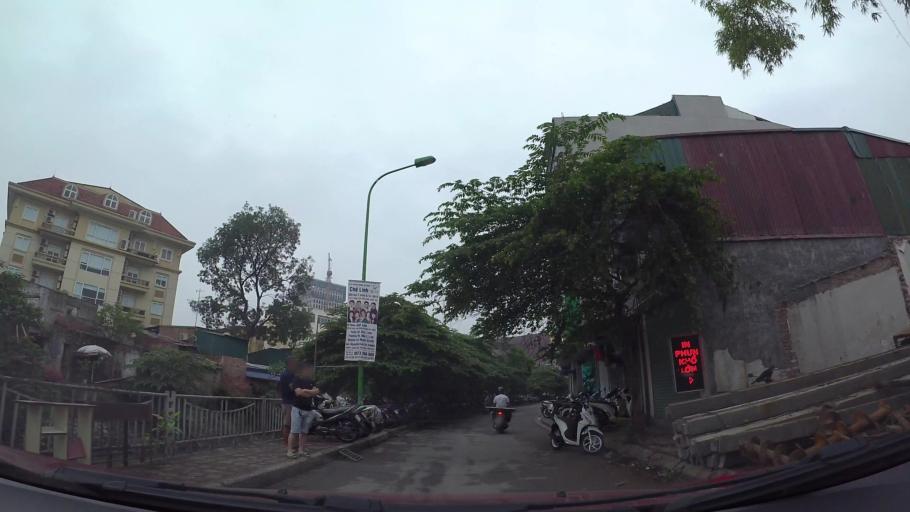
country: VN
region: Ha Noi
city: Dong Da
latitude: 21.0034
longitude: 105.8326
